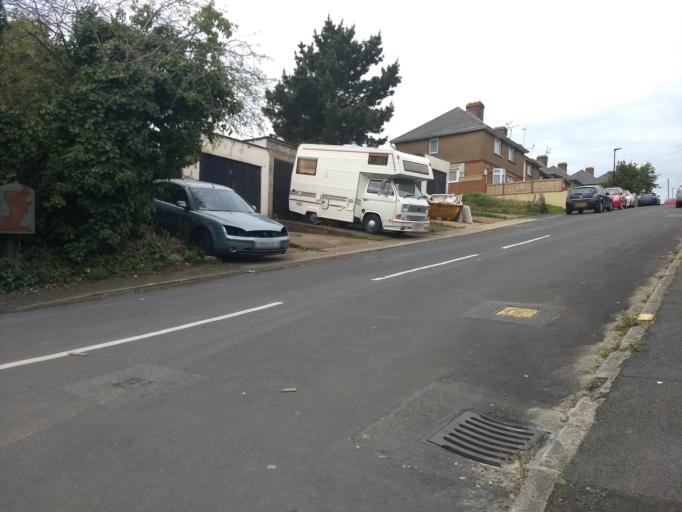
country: GB
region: England
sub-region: Isle of Wight
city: Ryde
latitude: 50.7215
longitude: -1.1602
